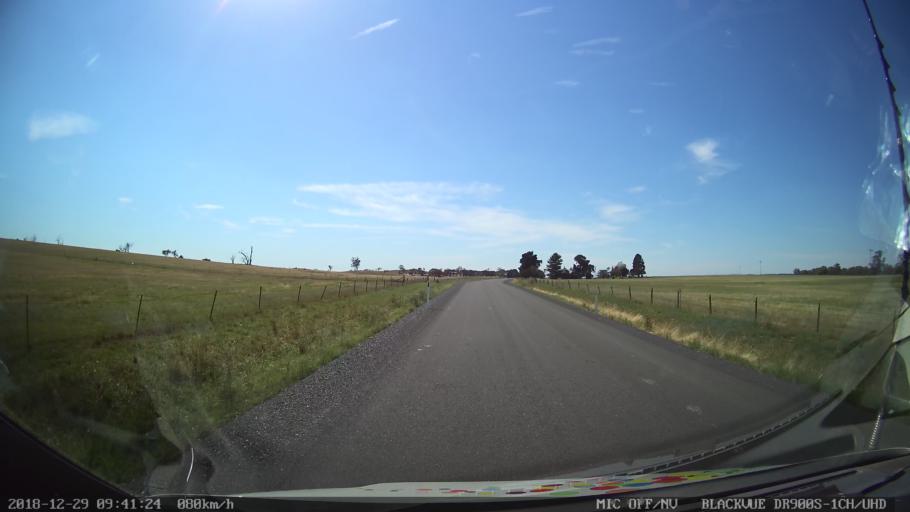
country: AU
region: New South Wales
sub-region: Upper Lachlan Shire
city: Crookwell
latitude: -34.6605
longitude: 149.4106
